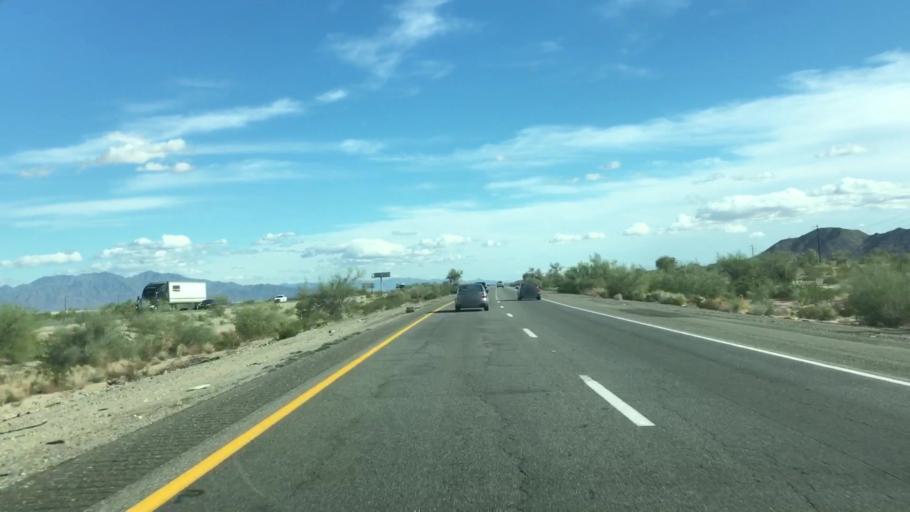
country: US
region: California
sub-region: Imperial County
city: Niland
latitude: 33.7103
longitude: -115.3779
